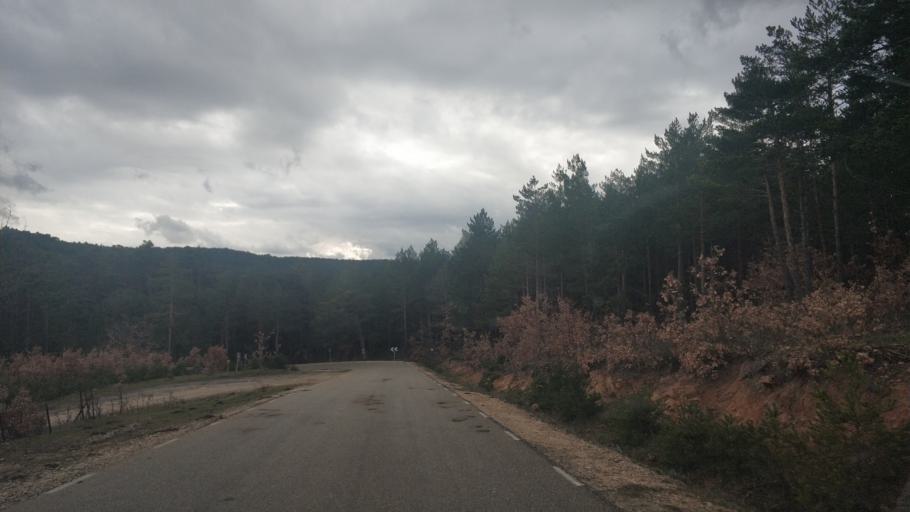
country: ES
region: Castille and Leon
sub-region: Provincia de Burgos
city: Canicosa de la Sierra
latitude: 41.9194
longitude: -3.0386
